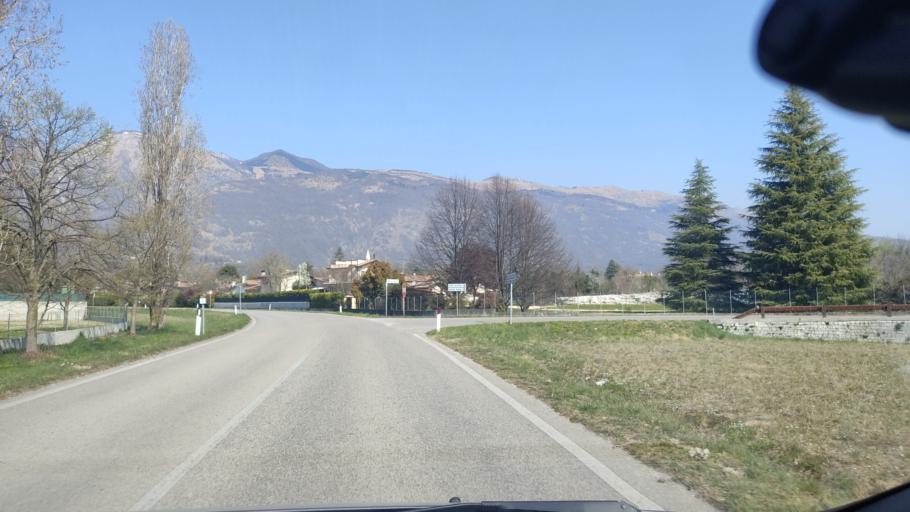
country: IT
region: Friuli Venezia Giulia
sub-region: Provincia di Pordenone
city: Budoia
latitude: 46.0468
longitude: 12.5373
